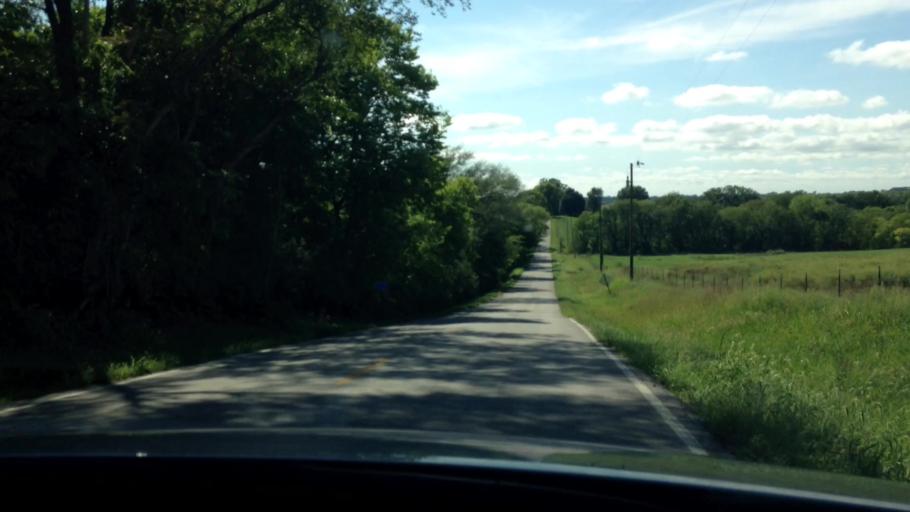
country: US
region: Missouri
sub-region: Clay County
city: Smithville
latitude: 39.3402
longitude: -94.6618
